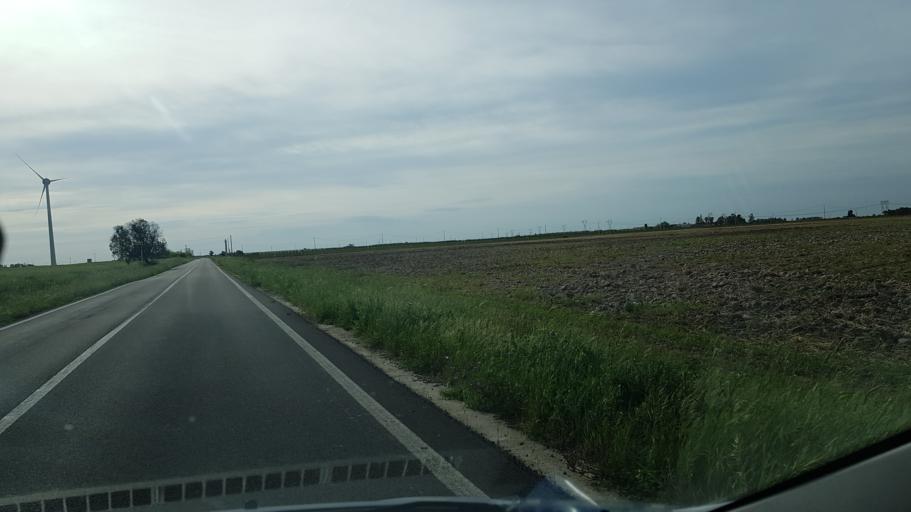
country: IT
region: Apulia
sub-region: Provincia di Brindisi
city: Tuturano
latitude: 40.5285
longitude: 17.9039
